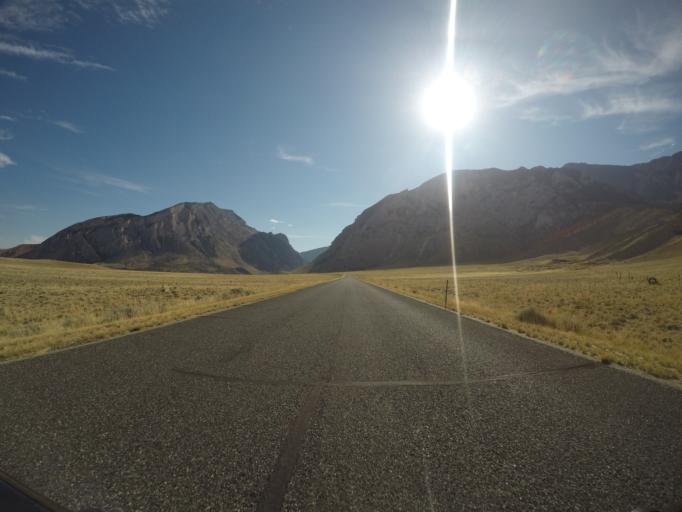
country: US
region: Montana
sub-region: Carbon County
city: Red Lodge
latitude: 44.8648
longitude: -109.2820
